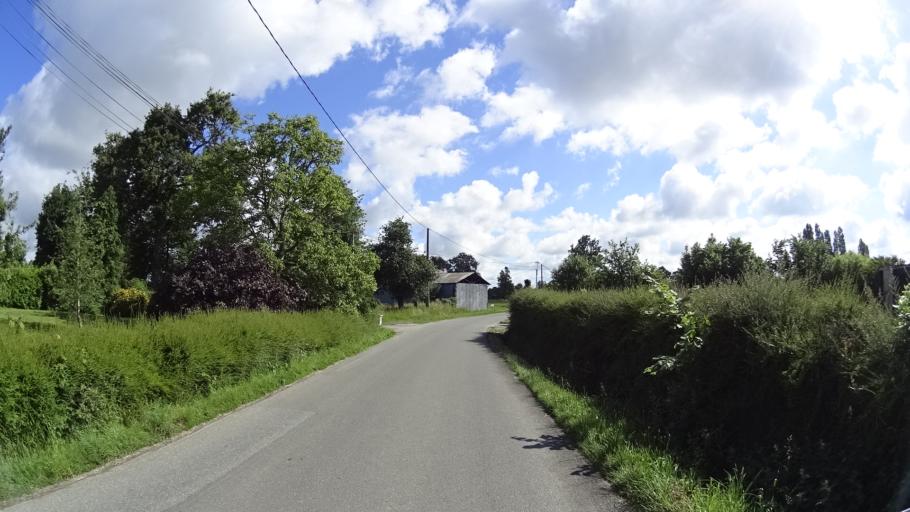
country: FR
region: Brittany
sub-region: Departement d'Ille-et-Vilaine
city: Saint-Gilles
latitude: 48.1330
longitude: -1.8146
